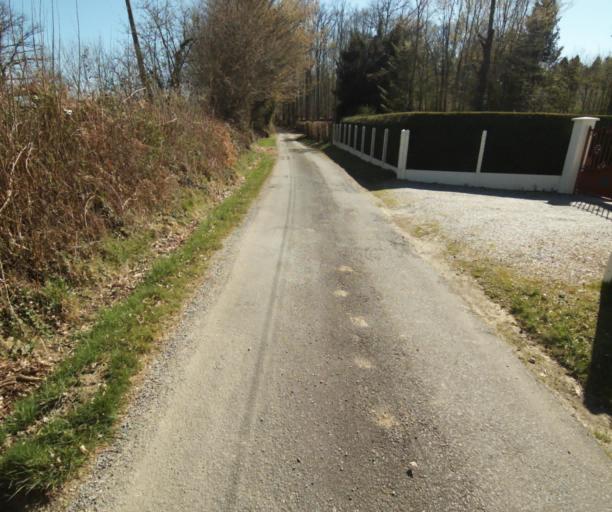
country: FR
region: Limousin
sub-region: Departement de la Correze
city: Chamboulive
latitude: 45.4571
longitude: 1.7286
